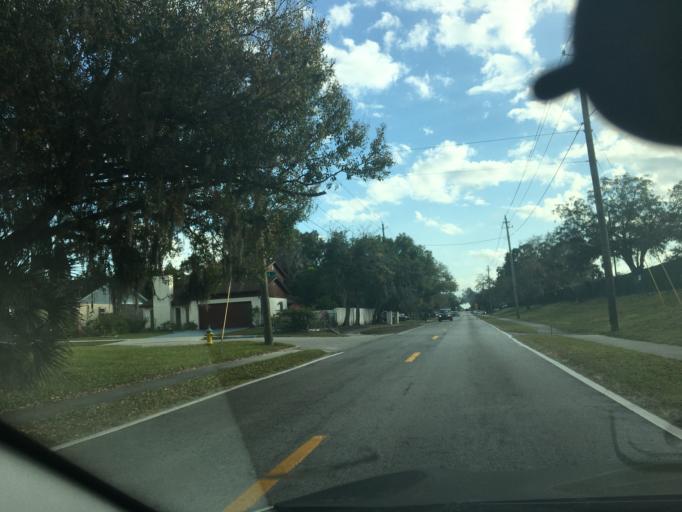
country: US
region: Florida
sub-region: Hillsborough County
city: Temple Terrace
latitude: 28.0420
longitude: -82.4099
